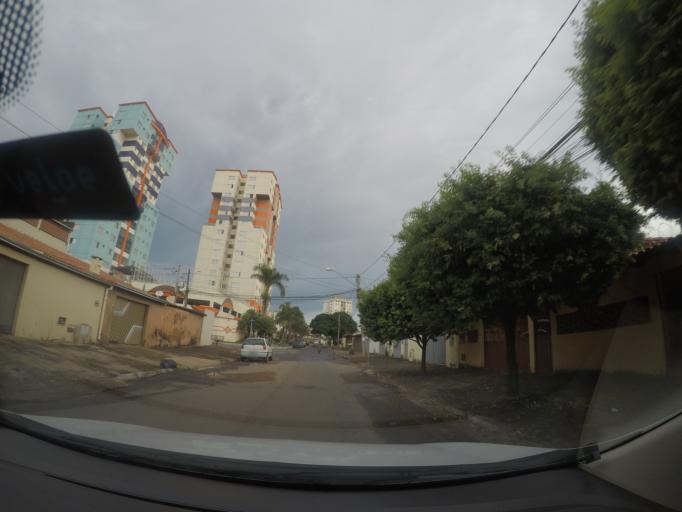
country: BR
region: Goias
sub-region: Goiania
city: Goiania
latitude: -16.6864
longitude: -49.3010
